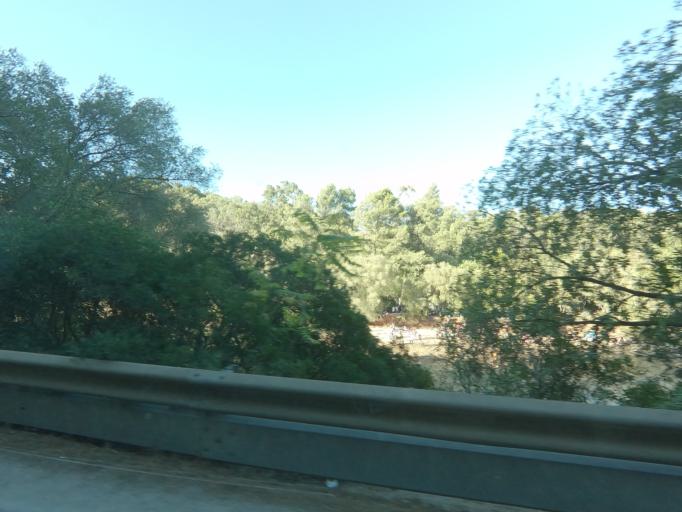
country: PT
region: Setubal
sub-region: Setubal
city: Setubal
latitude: 38.5073
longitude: -8.9271
